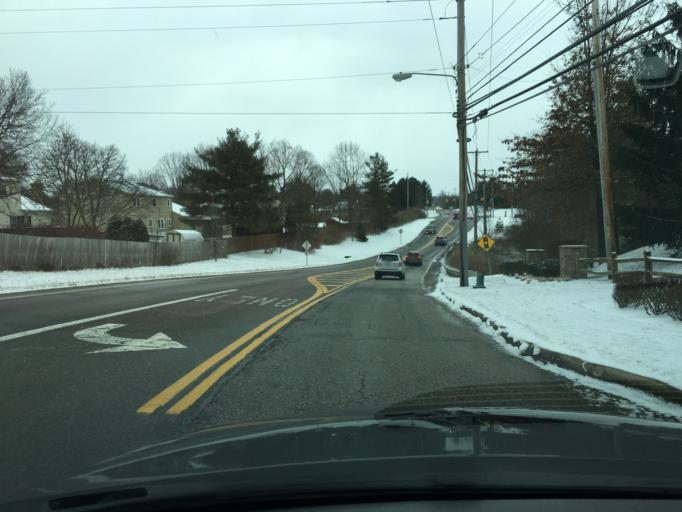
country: US
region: Ohio
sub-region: Summit County
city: Fairlawn
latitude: 41.1406
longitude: -81.5899
